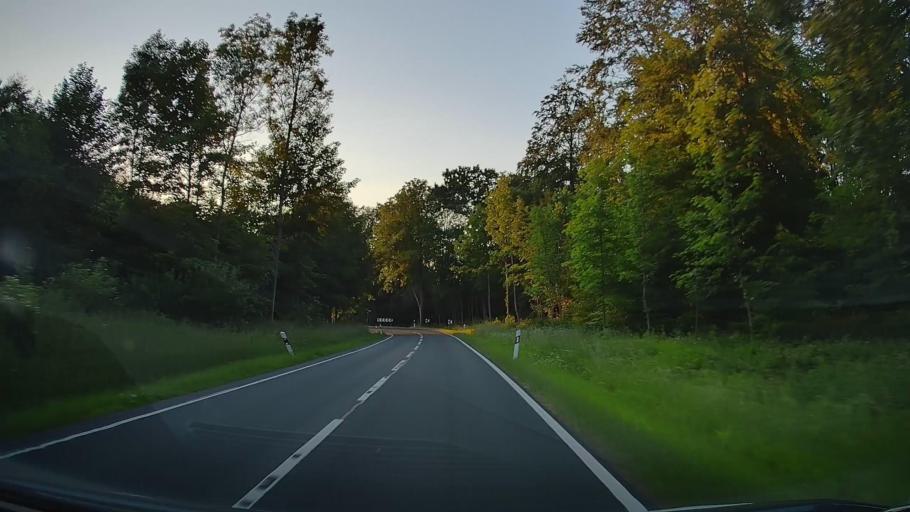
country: DE
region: Lower Saxony
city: Bad Pyrmont
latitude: 52.0025
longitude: 9.2112
